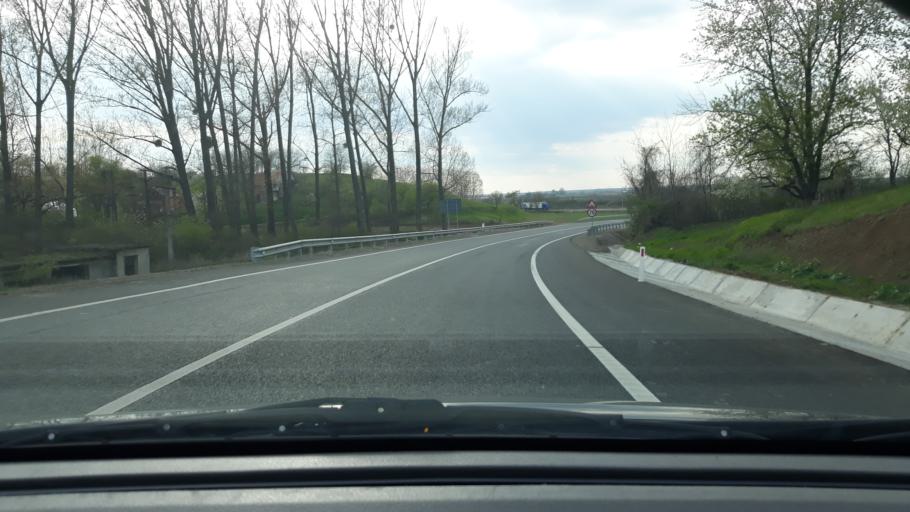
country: RO
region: Bihor
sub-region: Comuna Sacueni
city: Cadea
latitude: 47.3280
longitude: 22.0826
